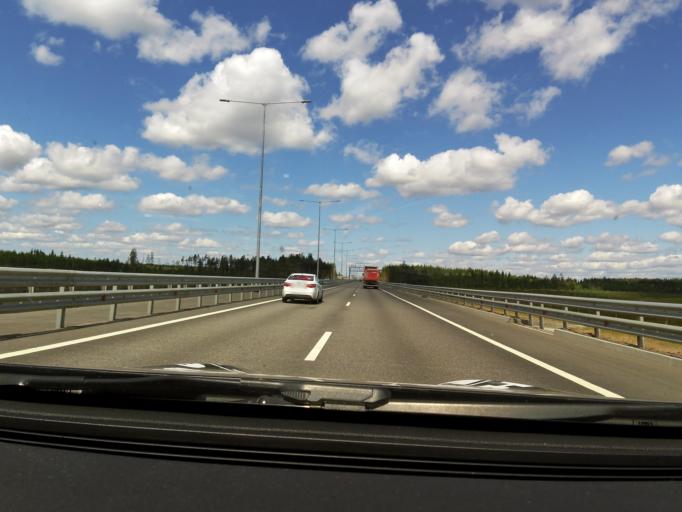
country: RU
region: Tverskaya
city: Krasnomayskiy
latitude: 57.6907
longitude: 34.2137
